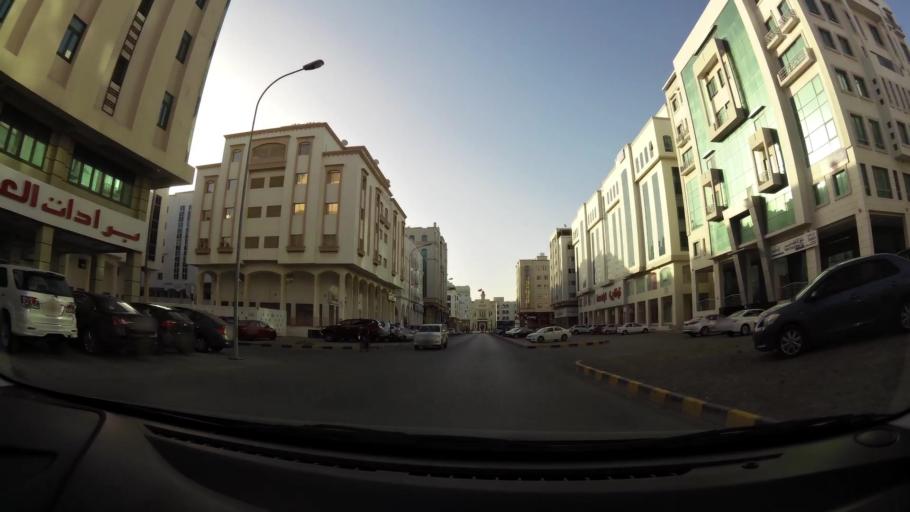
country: OM
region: Muhafazat Masqat
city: Muscat
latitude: 23.5922
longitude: 58.5518
